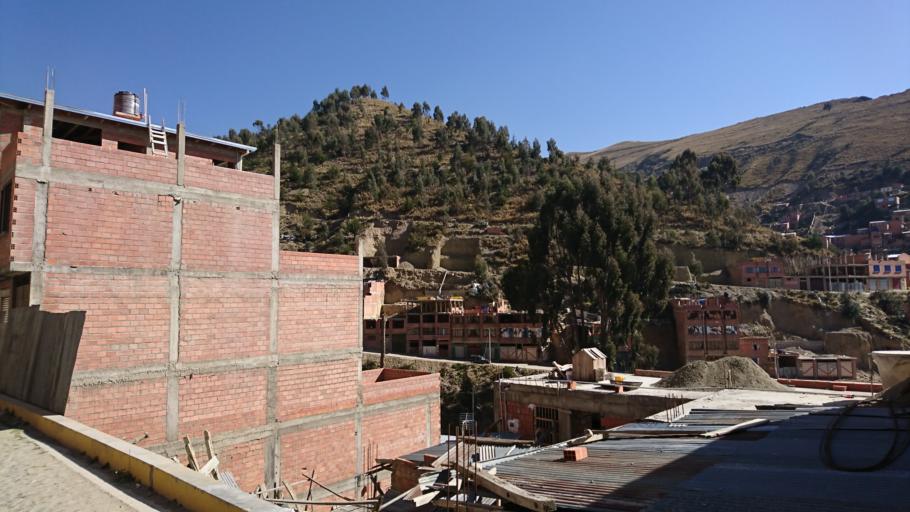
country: BO
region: La Paz
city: La Paz
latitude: -16.4688
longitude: -68.1255
